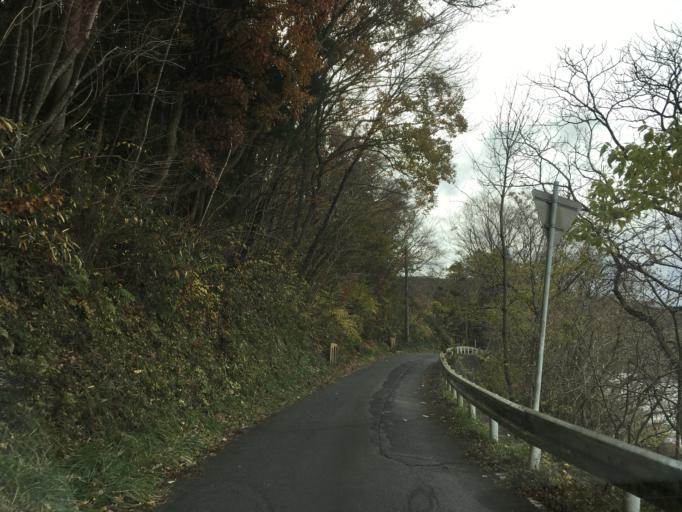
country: JP
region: Iwate
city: Ichinoseki
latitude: 38.7864
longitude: 141.2646
